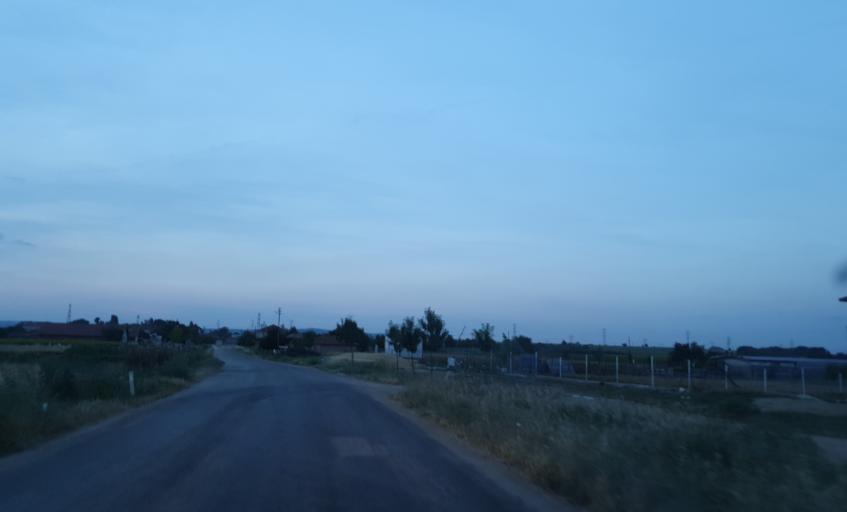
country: TR
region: Kirklareli
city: Vize
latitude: 41.4819
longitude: 27.7519
